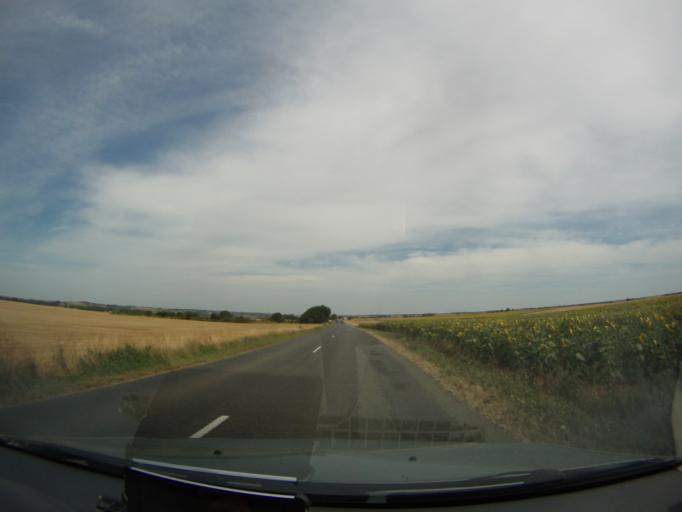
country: FR
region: Poitou-Charentes
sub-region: Departement de la Vienne
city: Saint-Jean-de-Sauves
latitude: 46.7980
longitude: 0.1043
